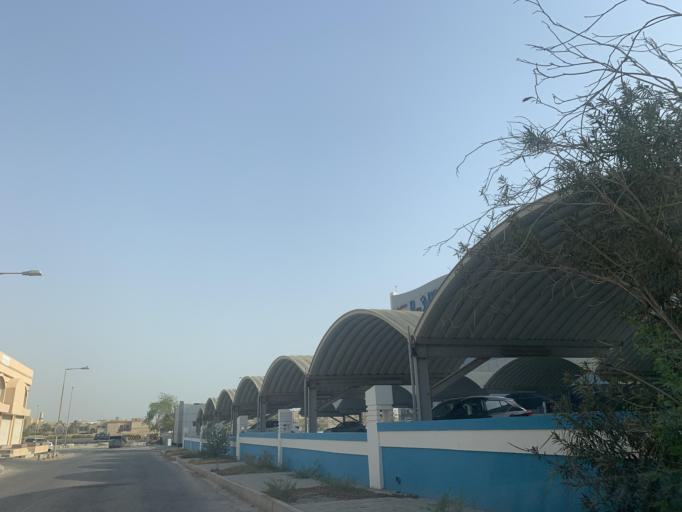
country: BH
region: Central Governorate
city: Madinat Hamad
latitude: 26.1743
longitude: 50.4697
